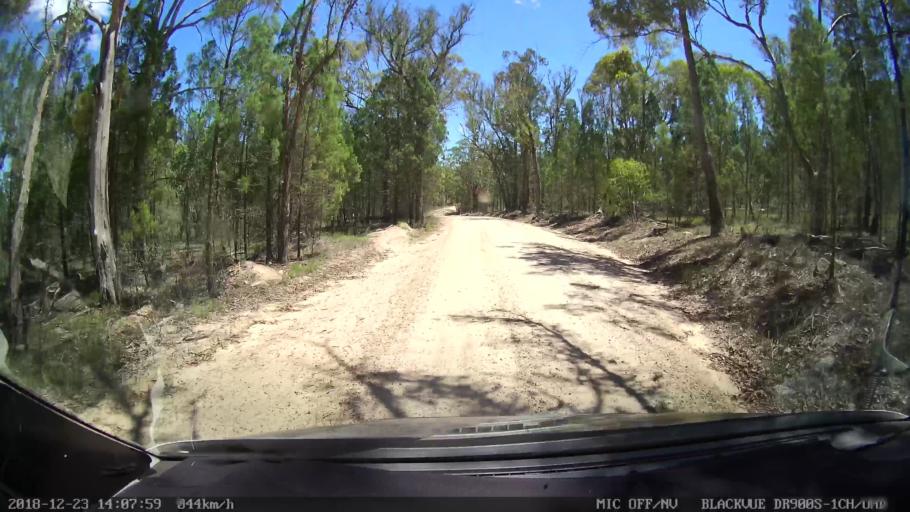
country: AU
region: New South Wales
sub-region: Tamworth Municipality
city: Manilla
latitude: -30.6395
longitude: 151.0703
